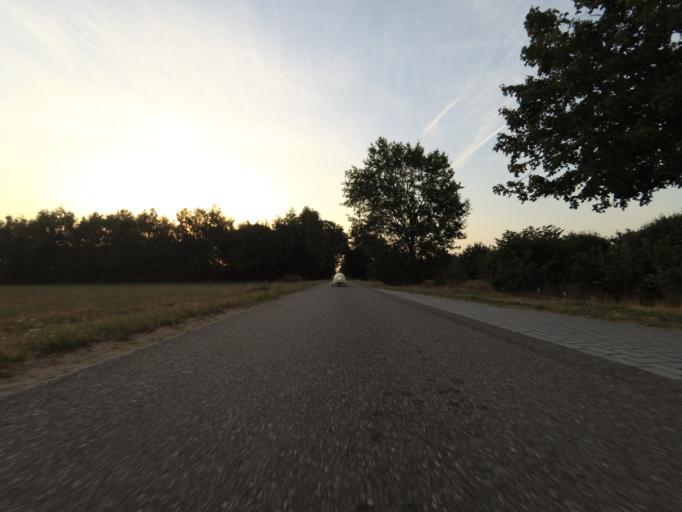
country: NL
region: Overijssel
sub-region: Gemeente Almelo
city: Almelo
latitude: 52.4104
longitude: 6.7106
